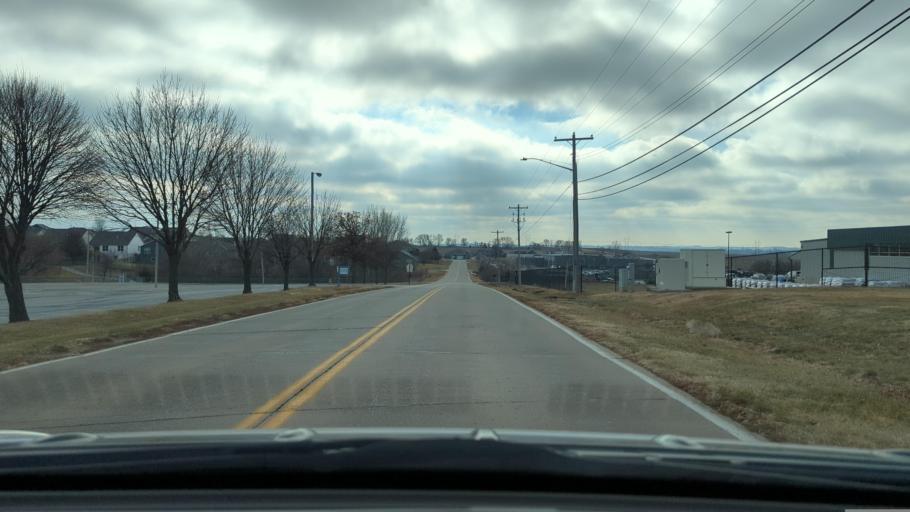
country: US
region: Nebraska
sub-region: Cass County
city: Plattsmouth
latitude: 40.9991
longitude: -95.9074
